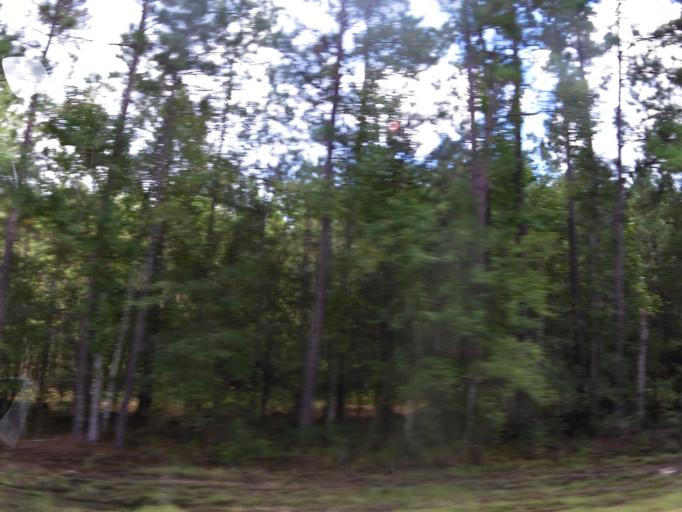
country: US
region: Georgia
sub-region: Brantley County
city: Nahunta
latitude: 31.0793
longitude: -82.0103
